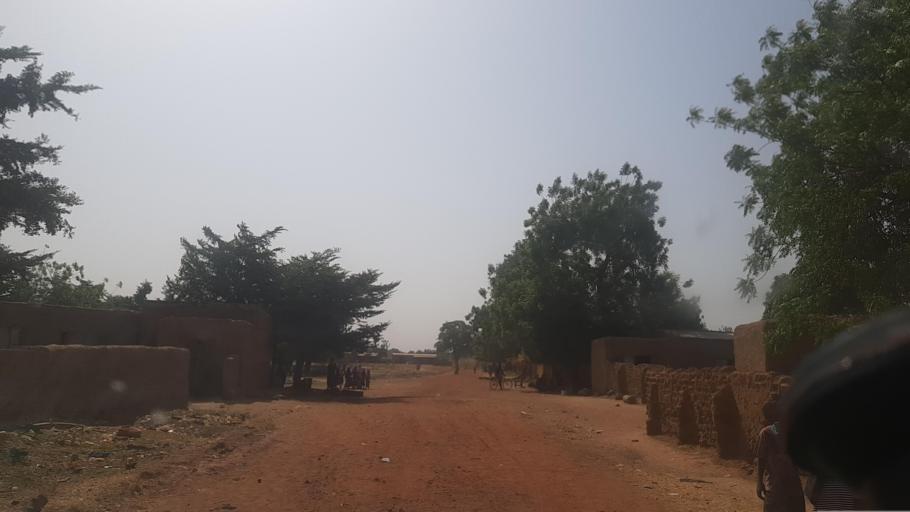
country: ML
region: Segou
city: Baroueli
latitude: 13.0116
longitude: -6.4226
